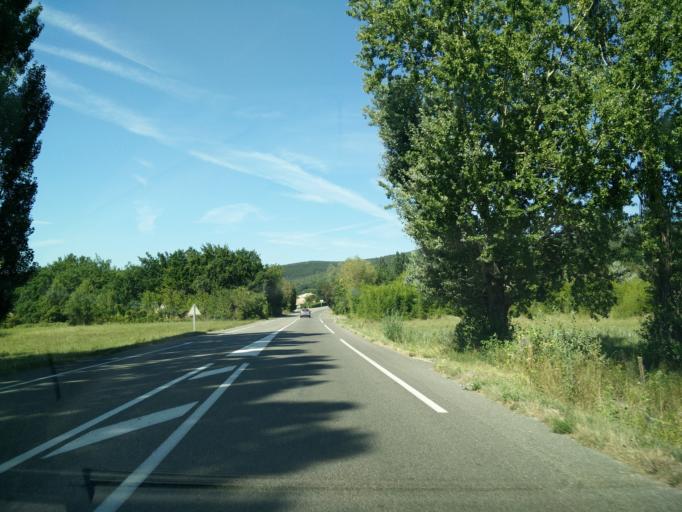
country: FR
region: Rhone-Alpes
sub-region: Departement de la Drome
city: Dieulefit
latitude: 44.5314
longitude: 5.0067
